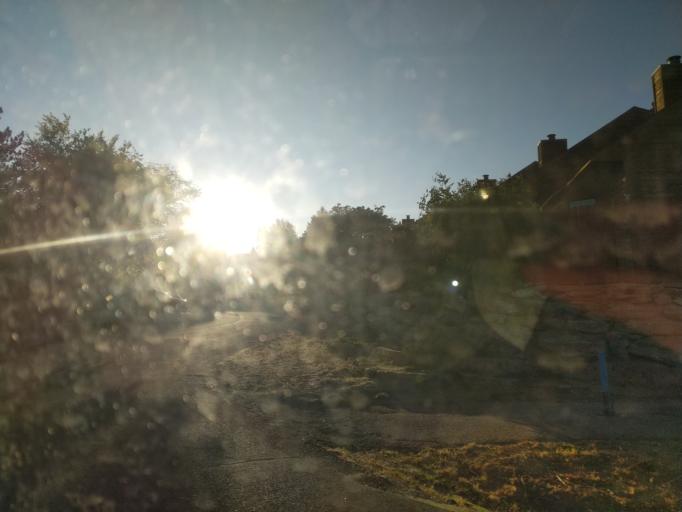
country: US
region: Colorado
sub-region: Mesa County
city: Redlands
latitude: 39.0601
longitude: -108.6101
